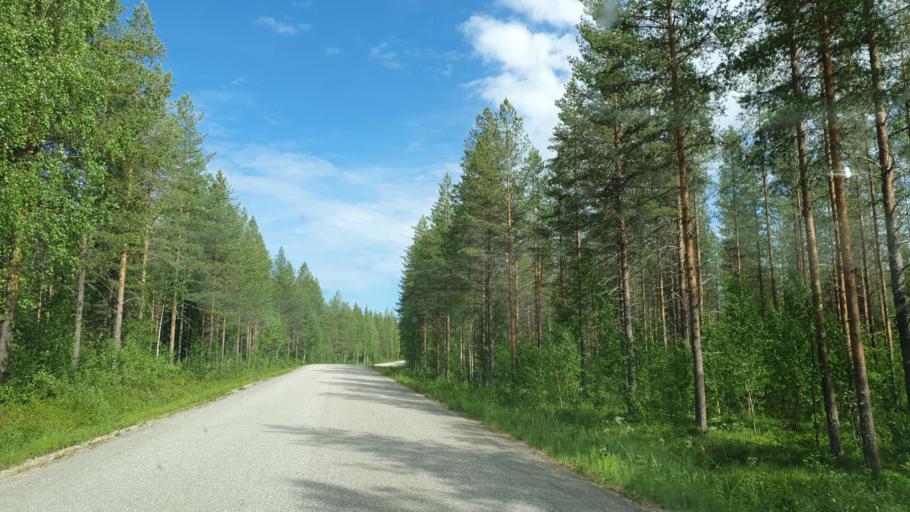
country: FI
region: Kainuu
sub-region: Kehys-Kainuu
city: Kuhmo
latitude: 64.5379
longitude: 29.3096
